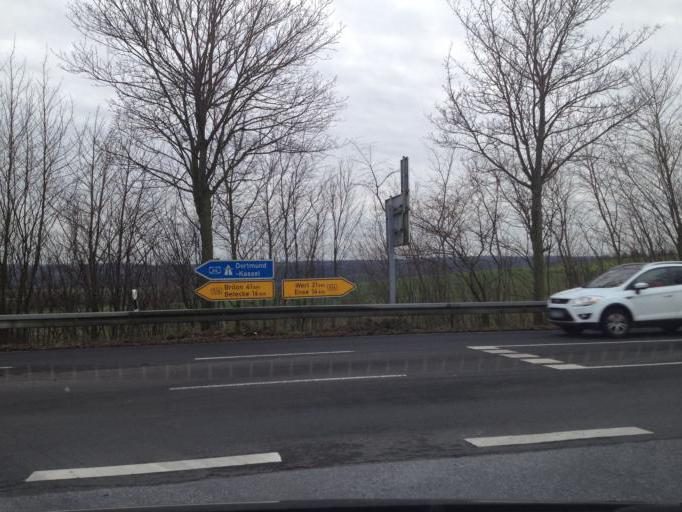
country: DE
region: North Rhine-Westphalia
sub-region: Regierungsbezirk Arnsberg
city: Mohnesee
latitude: 51.5061
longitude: 8.1690
